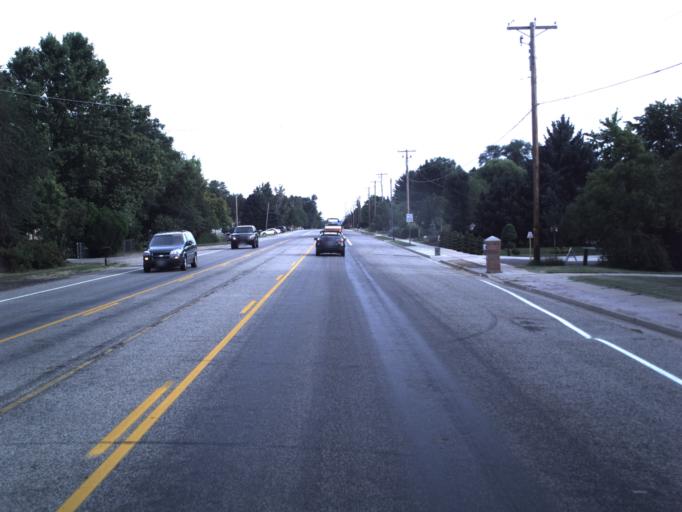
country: US
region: Utah
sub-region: Weber County
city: Farr West
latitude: 41.3044
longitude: -112.0277
